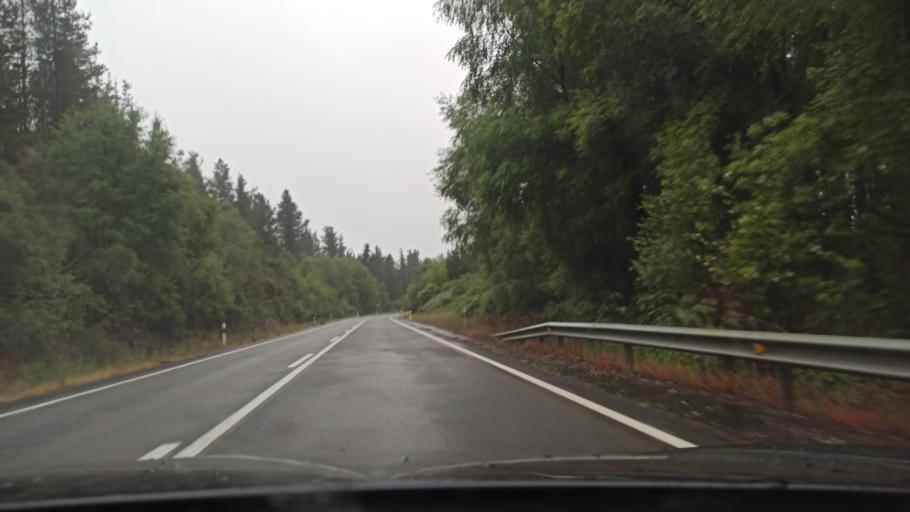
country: ES
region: Galicia
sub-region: Provincia de Lugo
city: Monterroso
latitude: 42.8201
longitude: -7.7624
